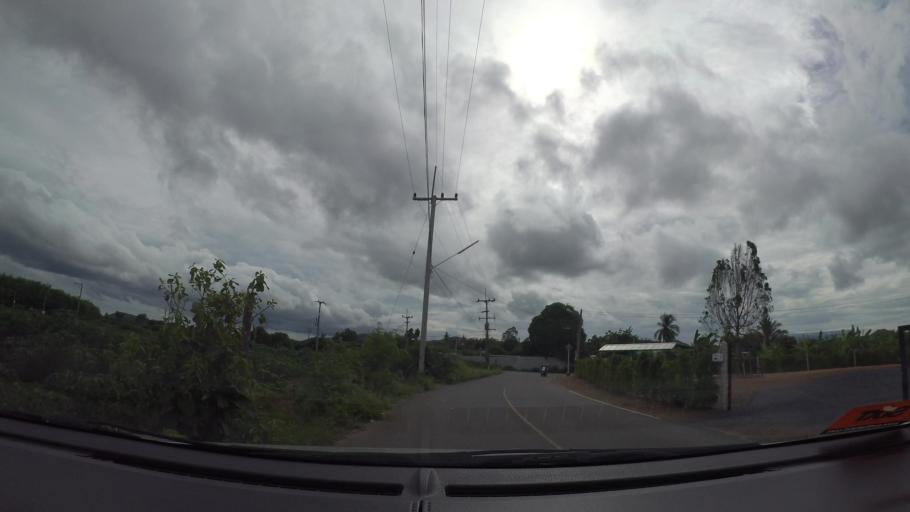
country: TH
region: Chon Buri
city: Sattahip
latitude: 12.7207
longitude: 100.9064
